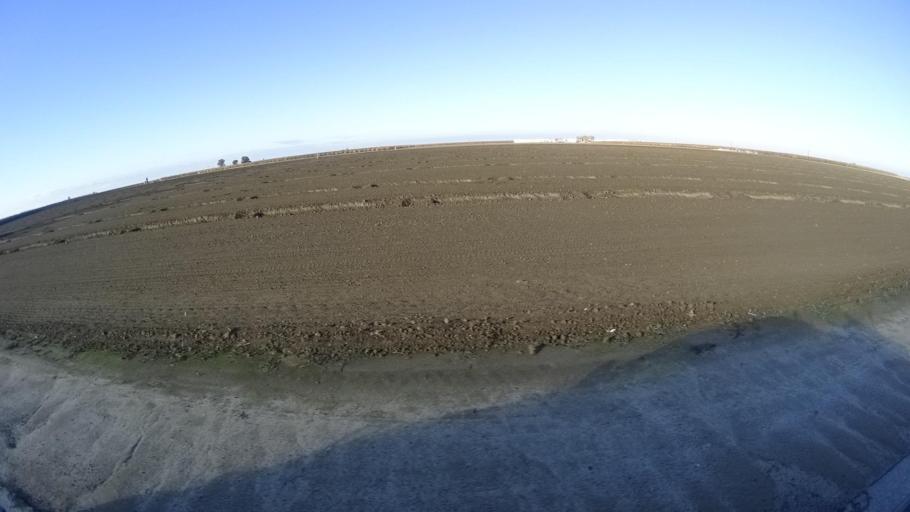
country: US
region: California
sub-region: Kern County
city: Delano
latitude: 35.7511
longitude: -119.3299
